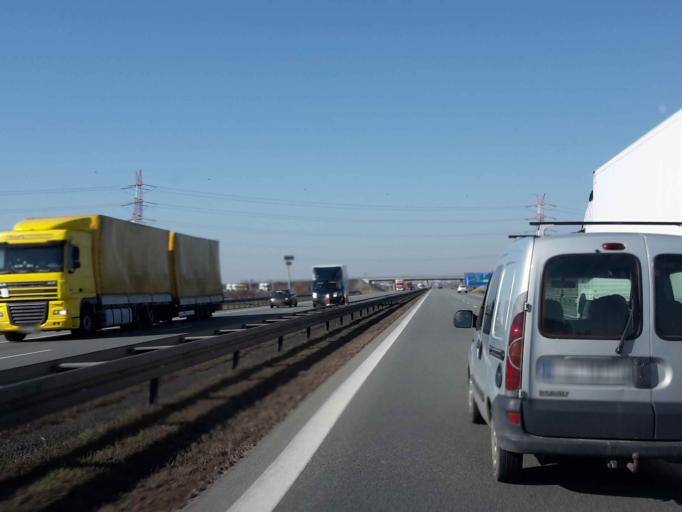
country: PL
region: Greater Poland Voivodeship
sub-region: Powiat poznanski
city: Komorniki
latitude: 52.3503
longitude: 16.8115
